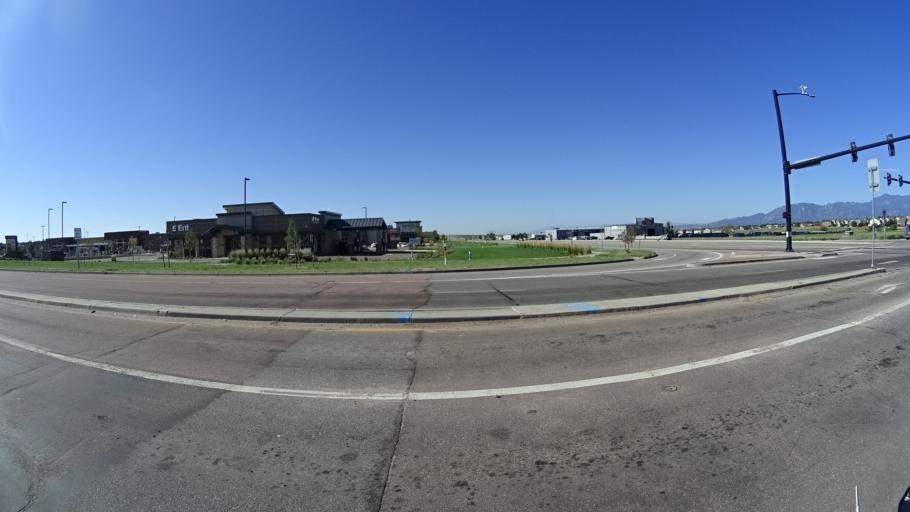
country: US
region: Colorado
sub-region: El Paso County
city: Cimarron Hills
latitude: 38.8683
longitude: -104.6826
